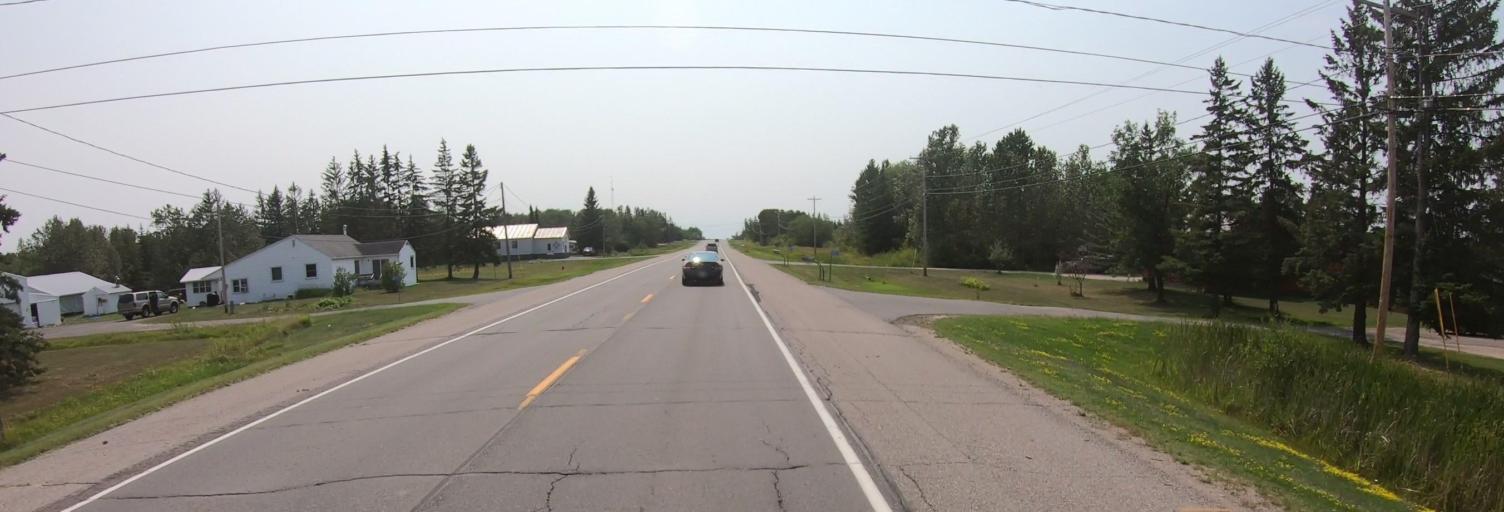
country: US
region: Minnesota
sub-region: Koochiching County
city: International Falls
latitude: 48.5738
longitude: -93.4402
